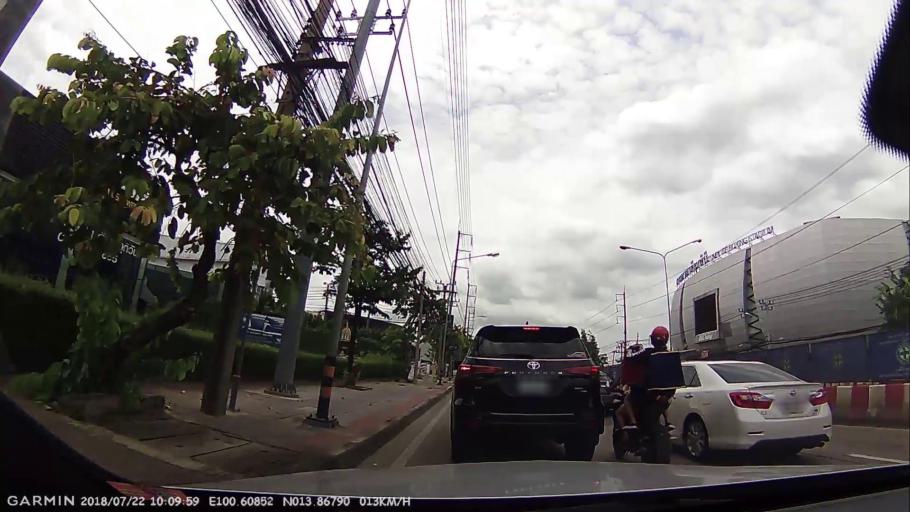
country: TH
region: Bangkok
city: Bang Khen
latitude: 13.8679
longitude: 100.6085
